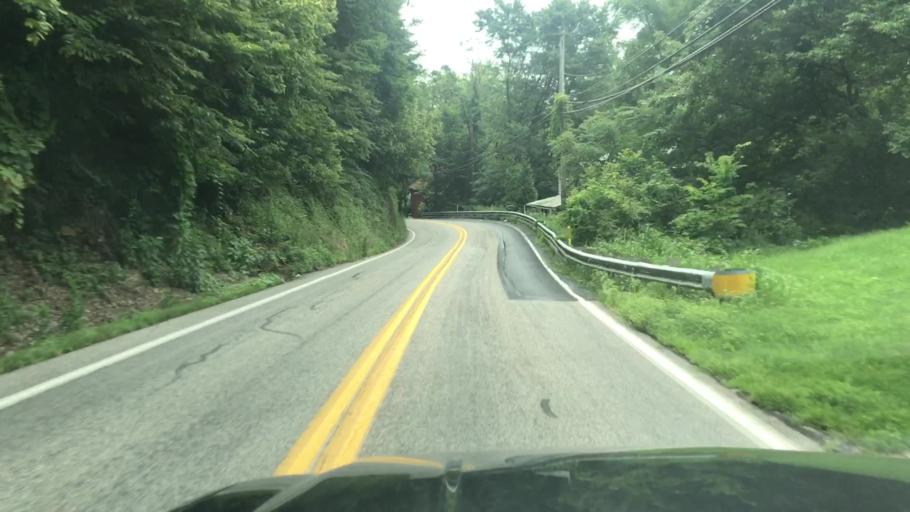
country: US
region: Pennsylvania
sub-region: Cumberland County
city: Shiremanstown
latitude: 40.2646
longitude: -76.9785
